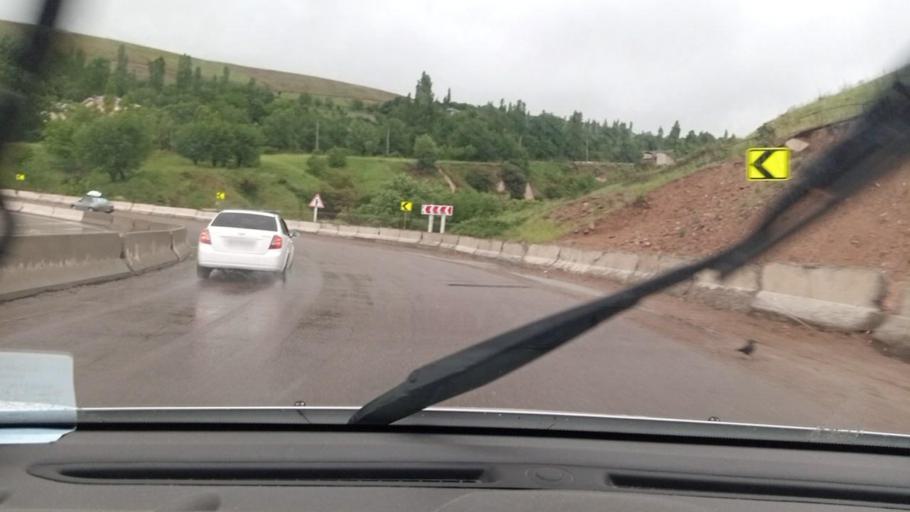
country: UZ
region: Toshkent
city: Angren
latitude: 41.0726
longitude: 70.2355
